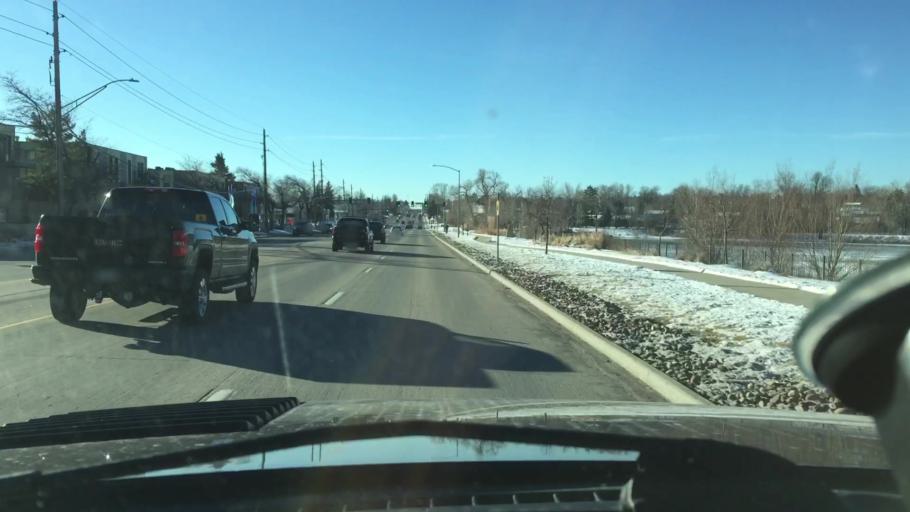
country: US
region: Colorado
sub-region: Adams County
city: Northglenn
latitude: 39.8906
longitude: -104.9968
